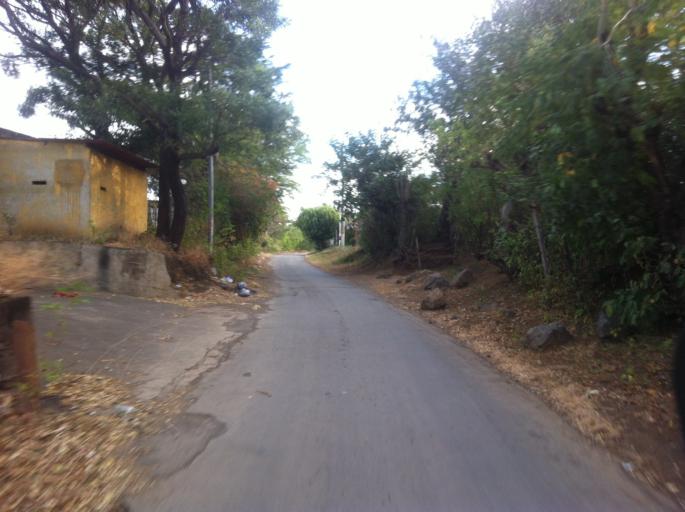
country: NI
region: Managua
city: Ciudad Sandino
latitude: 12.0956
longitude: -86.3139
